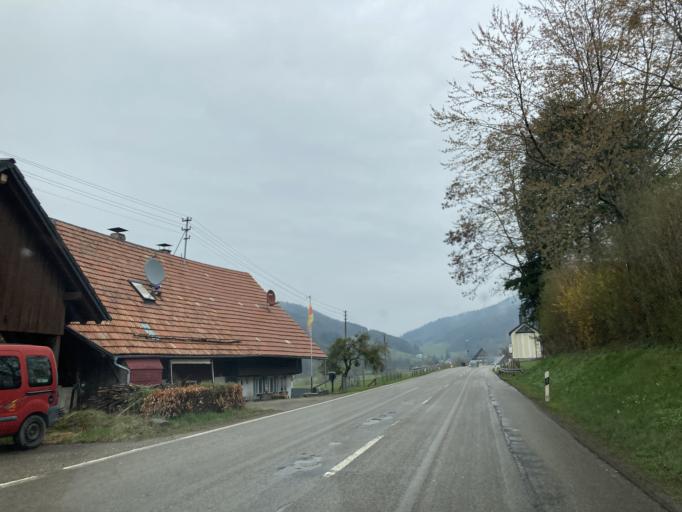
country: DE
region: Baden-Wuerttemberg
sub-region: Freiburg Region
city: Muhlenbach
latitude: 48.2078
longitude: 8.1271
